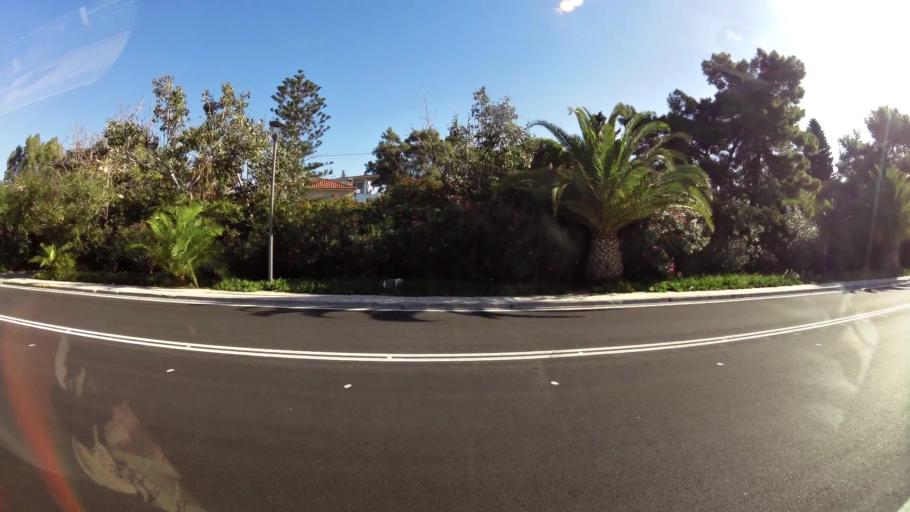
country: GR
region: Attica
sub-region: Nomarchia Athinas
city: Elliniko
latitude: 37.8728
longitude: 23.7341
